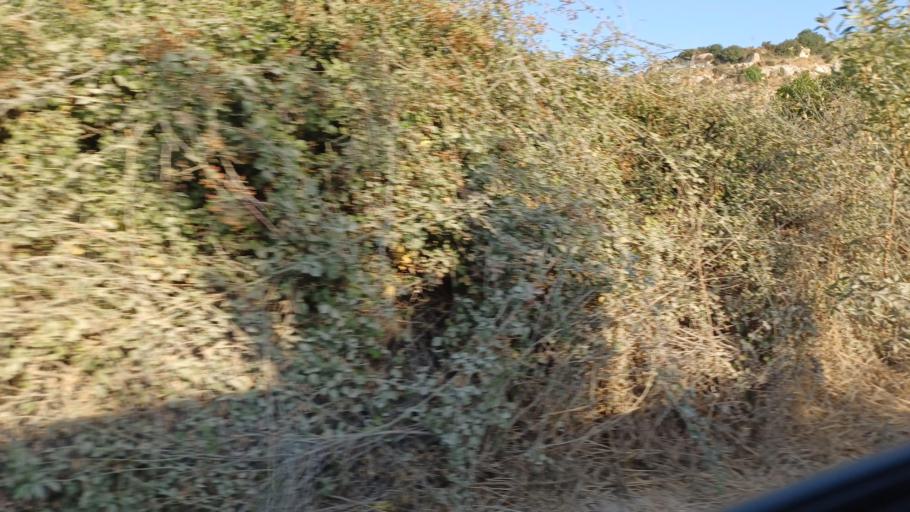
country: CY
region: Pafos
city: Tala
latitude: 34.8815
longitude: 32.4758
